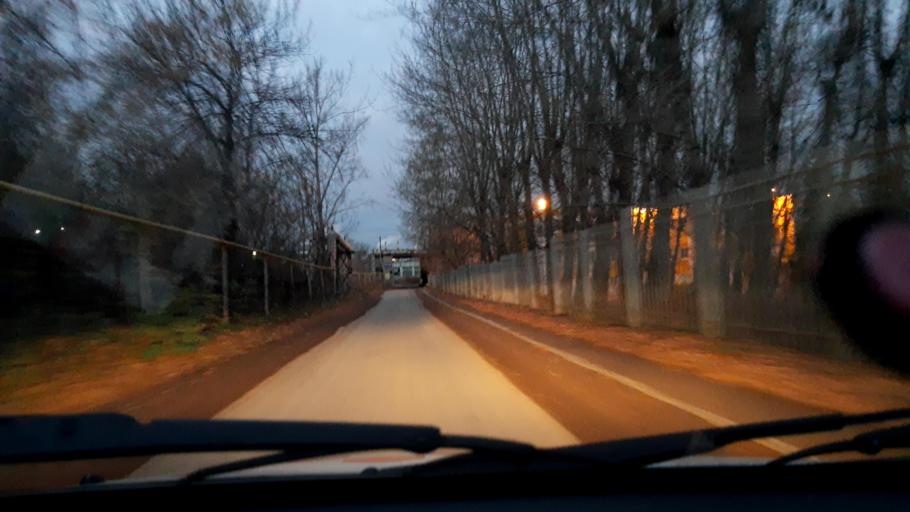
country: RU
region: Bashkortostan
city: Ufa
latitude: 54.8359
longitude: 56.1164
